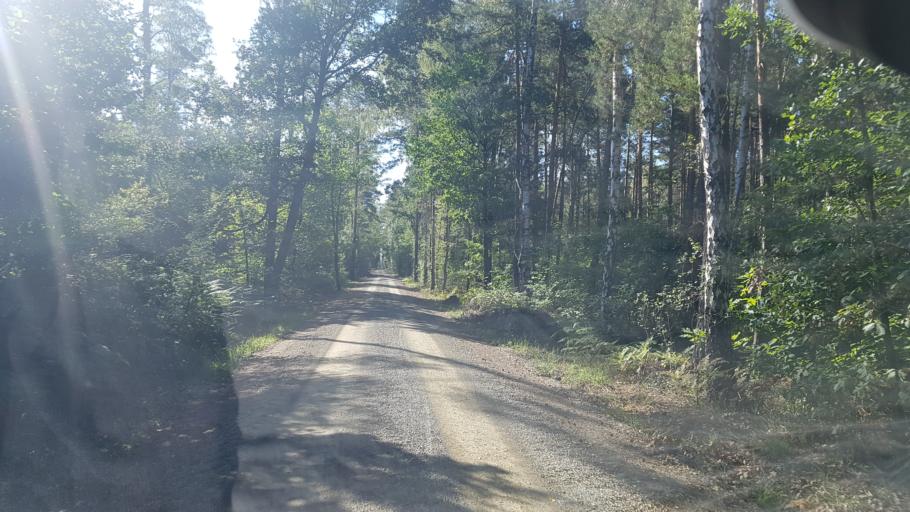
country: DE
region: Brandenburg
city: Ruckersdorf
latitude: 51.5442
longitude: 13.5807
